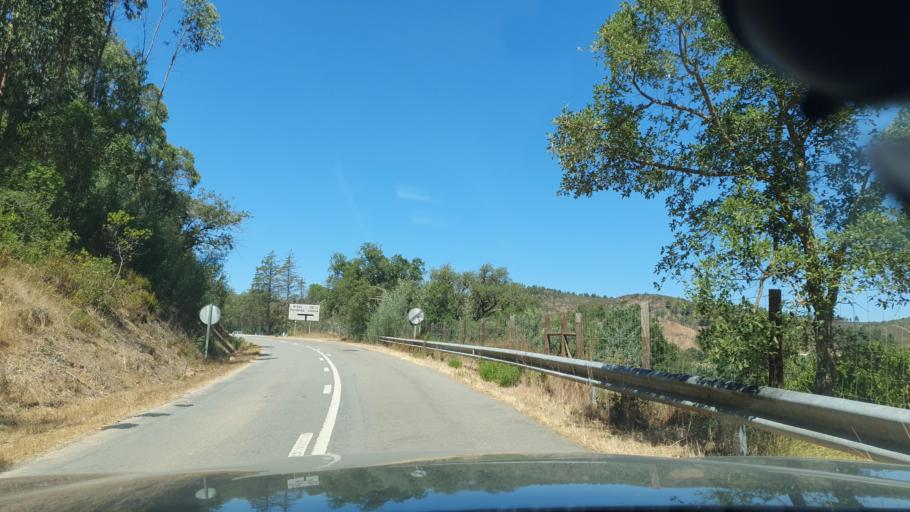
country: PT
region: Beja
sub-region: Odemira
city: Odemira
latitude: 37.5093
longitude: -8.4743
